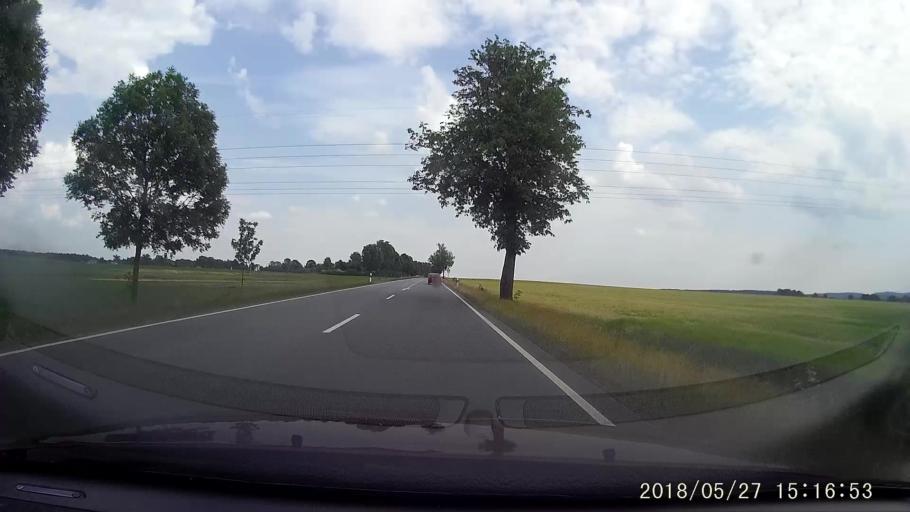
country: DE
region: Saxony
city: Niesky
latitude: 51.2746
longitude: 14.8315
